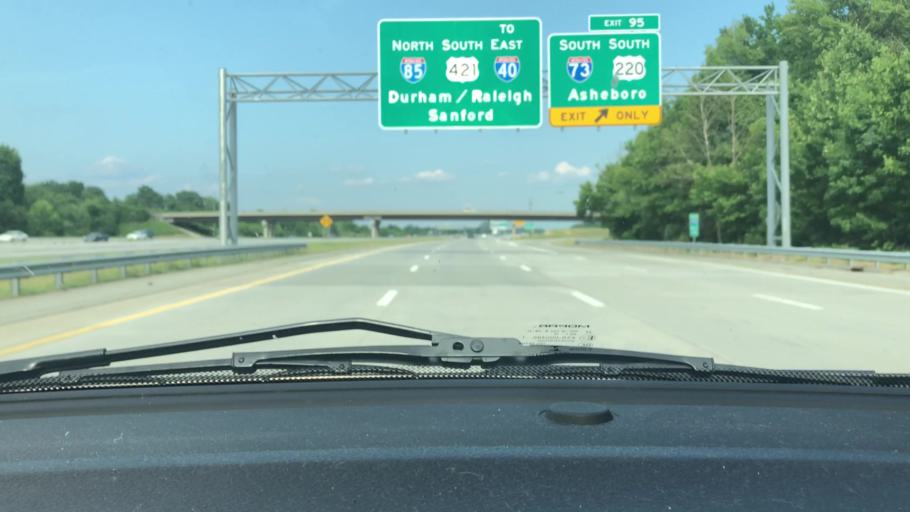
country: US
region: North Carolina
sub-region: Guilford County
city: Greensboro
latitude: 36.0033
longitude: -79.8364
